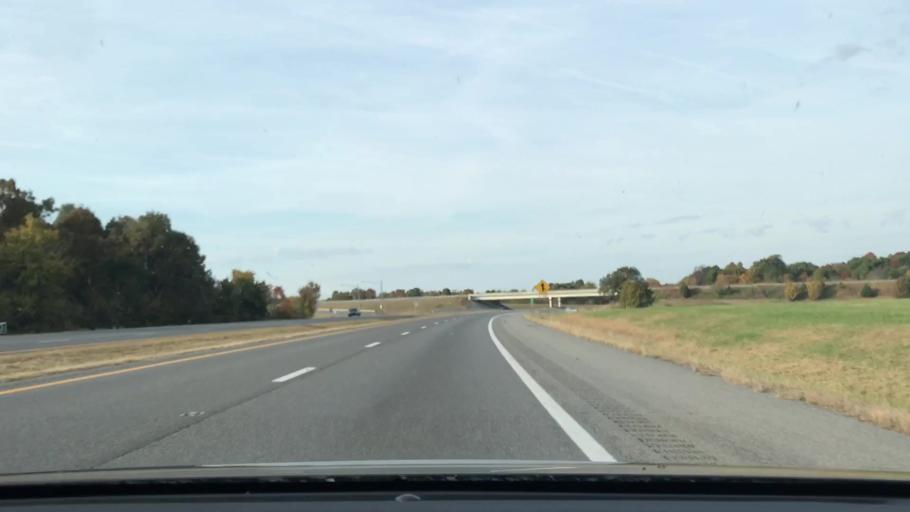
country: US
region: Kentucky
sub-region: Marshall County
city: Benton
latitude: 36.8496
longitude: -88.3754
